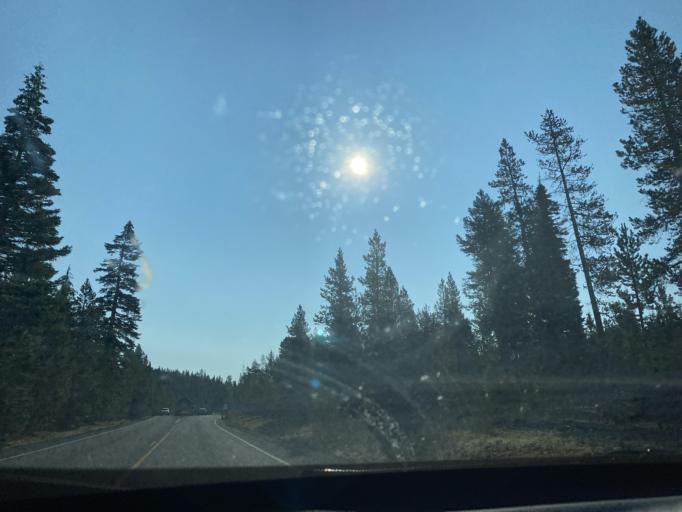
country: US
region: Oregon
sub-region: Deschutes County
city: Three Rivers
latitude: 43.7055
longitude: -121.3017
